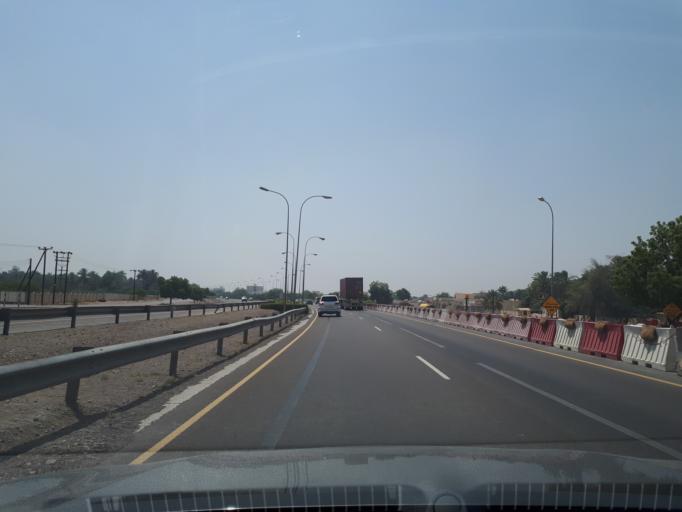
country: OM
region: Al Batinah
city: Al Sohar
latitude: 24.3924
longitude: 56.6934
